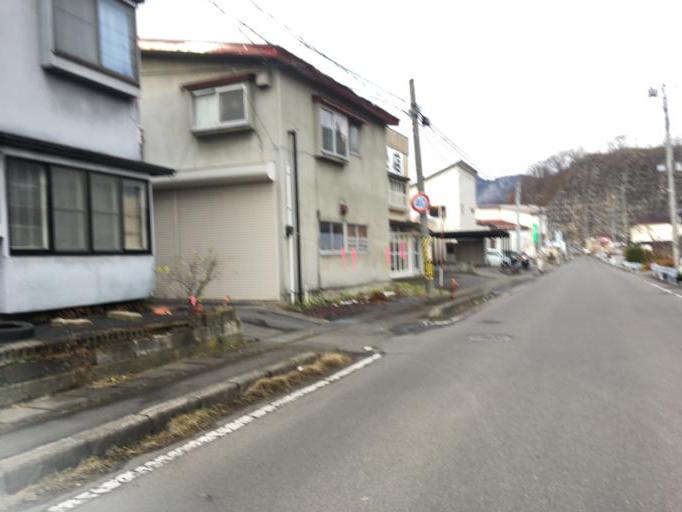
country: JP
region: Aomori
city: Hirosaki
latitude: 40.5225
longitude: 140.5662
